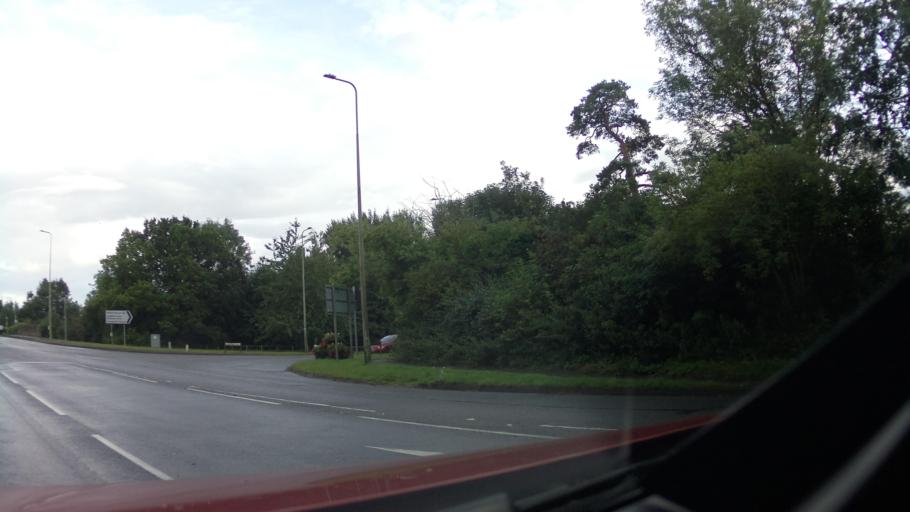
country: GB
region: England
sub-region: Oxfordshire
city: Kidlington
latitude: 51.8326
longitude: -1.3021
